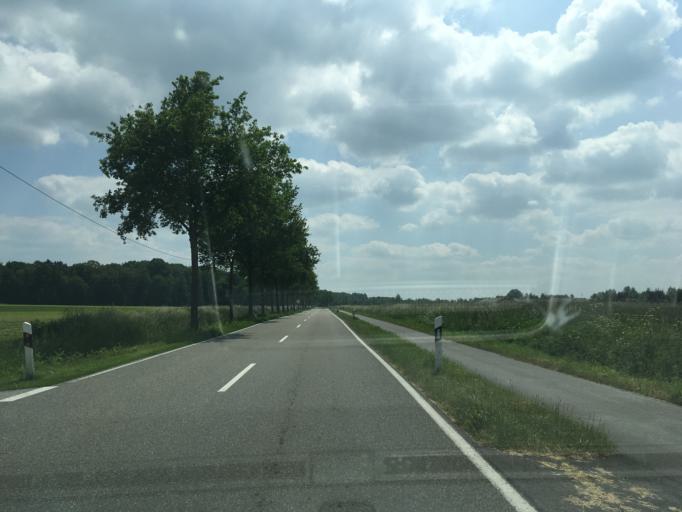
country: DE
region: North Rhine-Westphalia
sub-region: Regierungsbezirk Munster
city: Rhede
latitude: 51.8024
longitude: 6.7547
